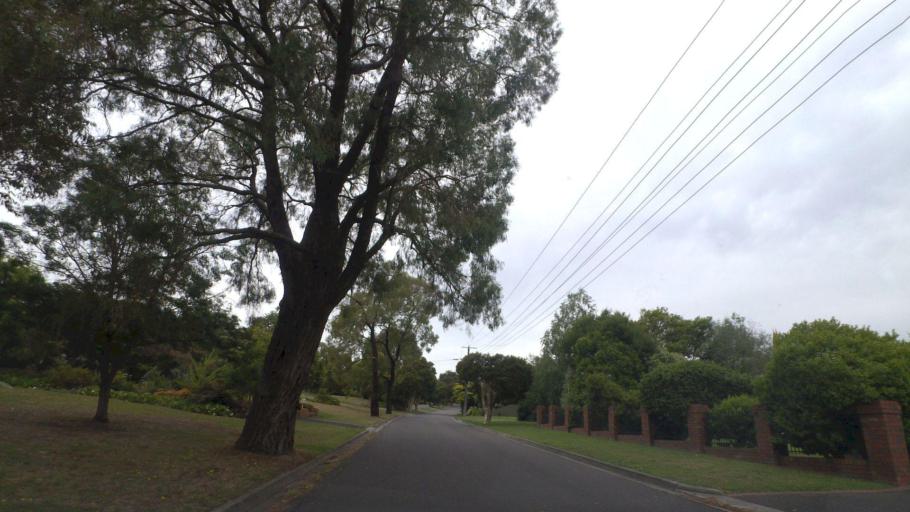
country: AU
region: Victoria
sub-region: Yarra Ranges
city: Lilydale
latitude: -37.7802
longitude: 145.3450
